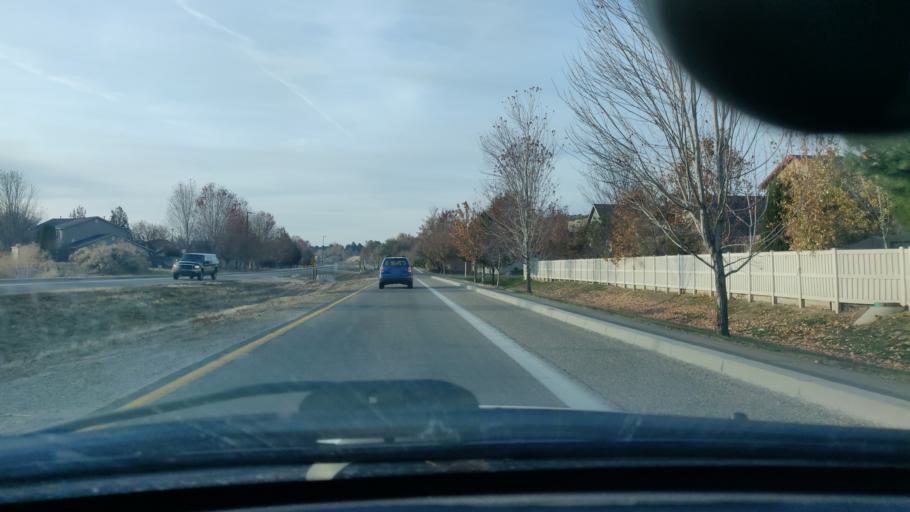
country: US
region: Idaho
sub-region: Ada County
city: Eagle
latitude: 43.6846
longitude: -116.2906
